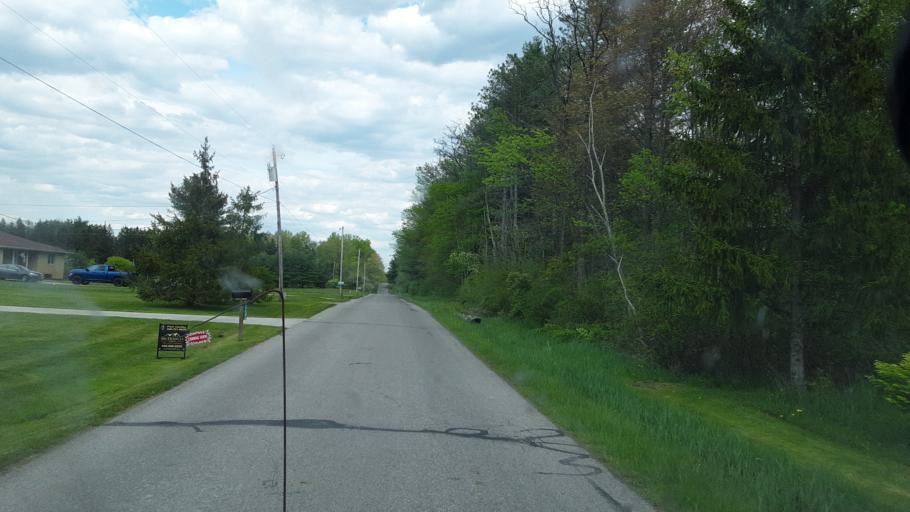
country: US
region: Ohio
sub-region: Portage County
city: Garrettsville
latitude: 41.3478
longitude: -81.0149
